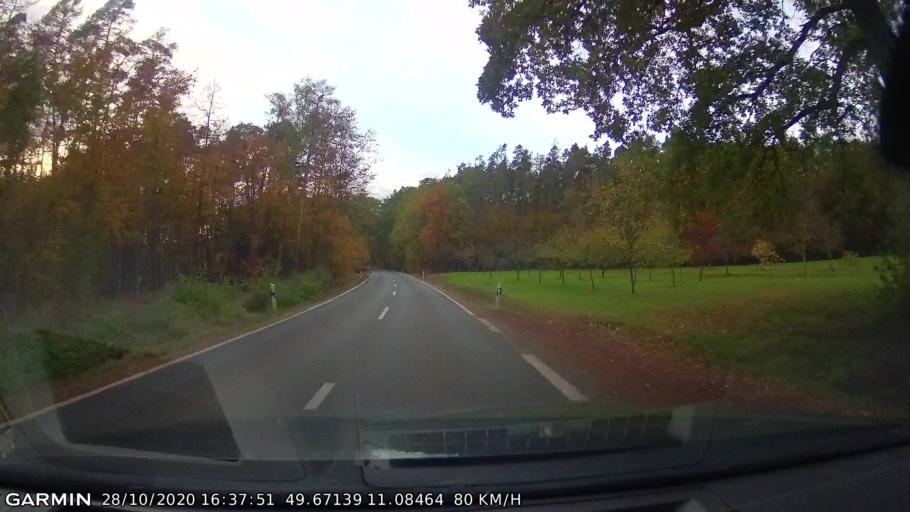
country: DE
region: Bavaria
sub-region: Upper Franconia
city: Effeltrich
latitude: 49.6716
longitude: 11.0844
